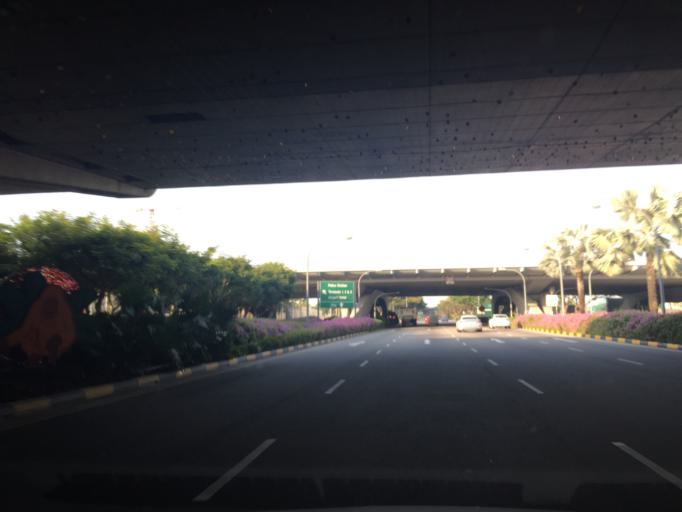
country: SG
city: Singapore
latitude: 1.3463
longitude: 103.9840
